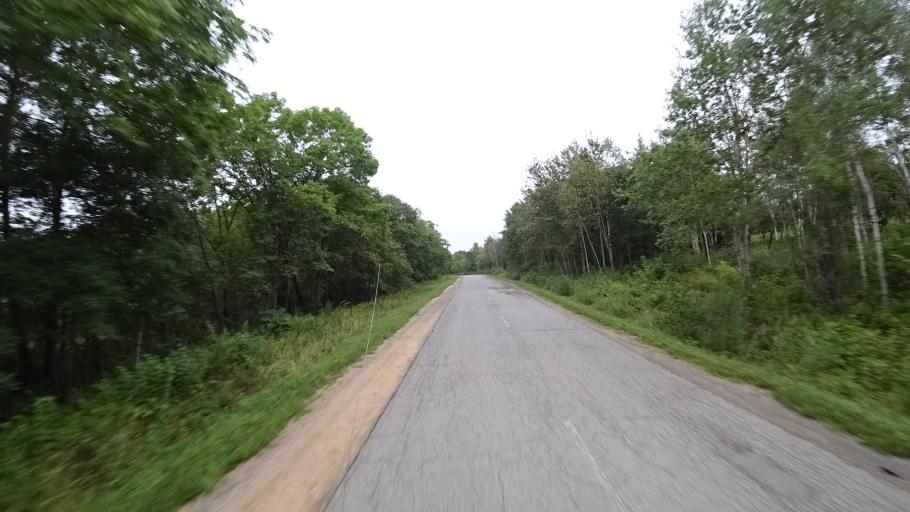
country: RU
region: Primorskiy
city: Rettikhovka
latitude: 44.1663
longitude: 132.7806
